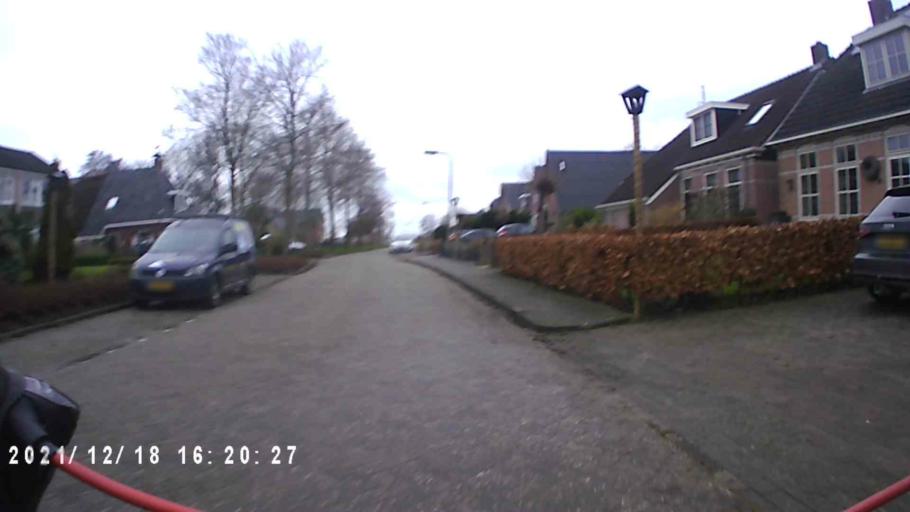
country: NL
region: Friesland
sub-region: Gemeente Dongeradeel
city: Anjum
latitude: 53.3792
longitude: 6.0511
